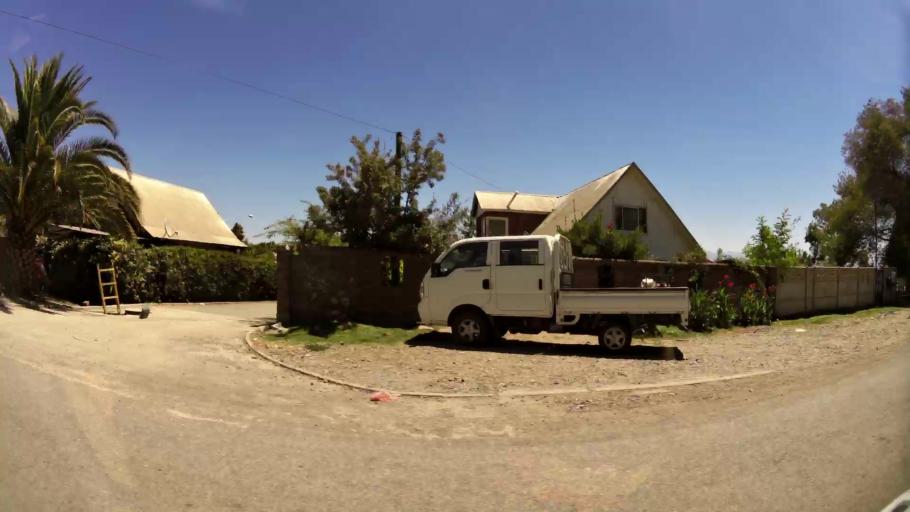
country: CL
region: O'Higgins
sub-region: Provincia de Cachapoal
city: Rancagua
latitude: -34.2223
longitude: -70.7825
